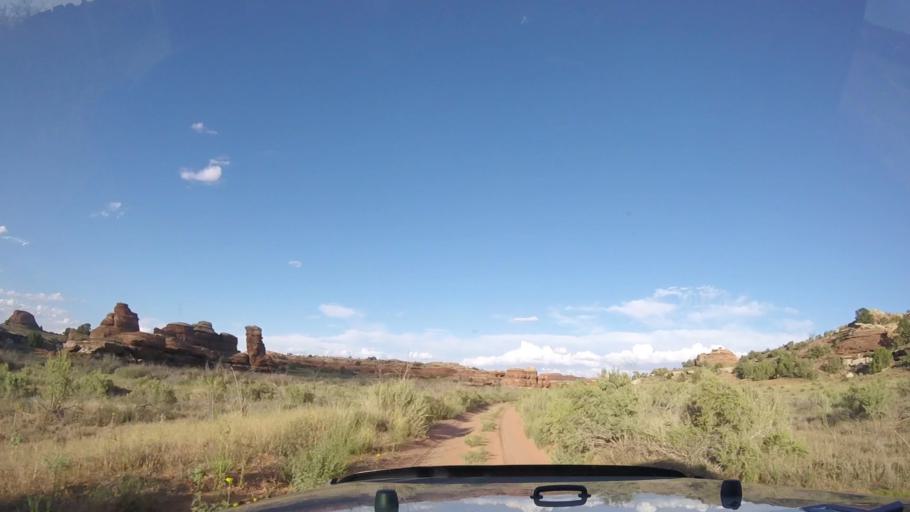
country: US
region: Utah
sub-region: Grand County
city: Moab
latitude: 38.1922
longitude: -109.7821
